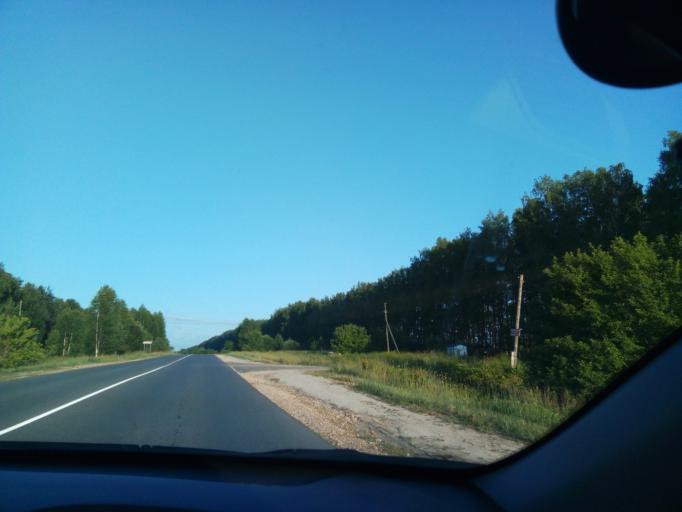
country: RU
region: Nizjnij Novgorod
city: Satis
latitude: 54.9009
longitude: 43.1378
